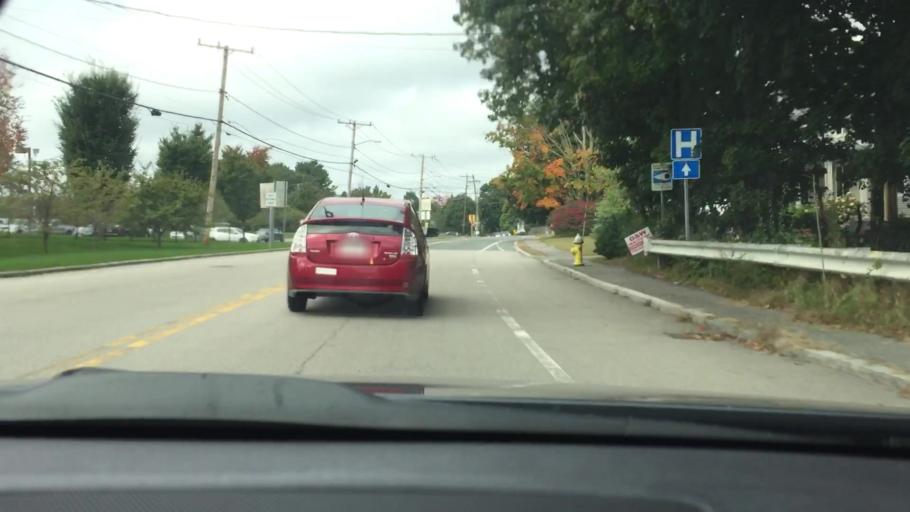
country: US
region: Massachusetts
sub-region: Norfolk County
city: Needham
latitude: 42.2702
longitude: -71.2036
